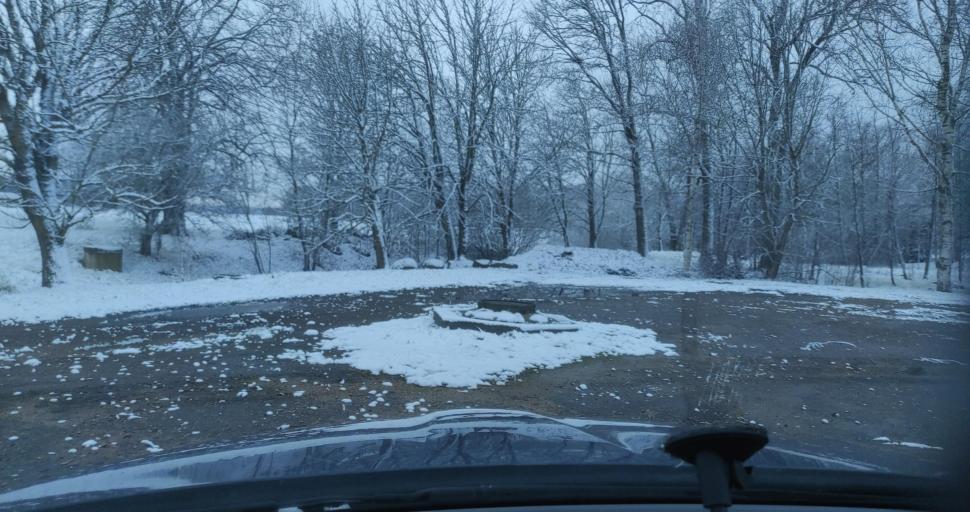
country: LV
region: Skrunda
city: Skrunda
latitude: 56.8734
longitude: 22.2321
